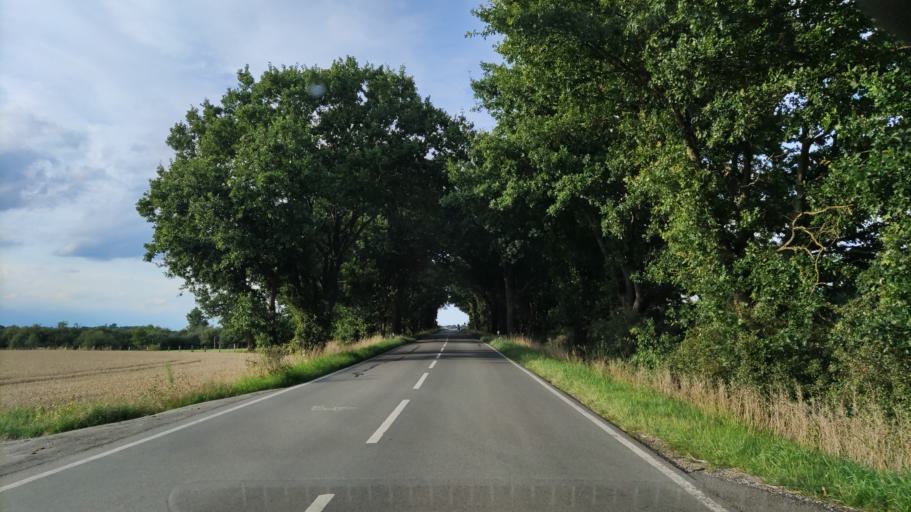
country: DE
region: Lower Saxony
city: Dannenberg
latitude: 53.1262
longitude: 11.1175
